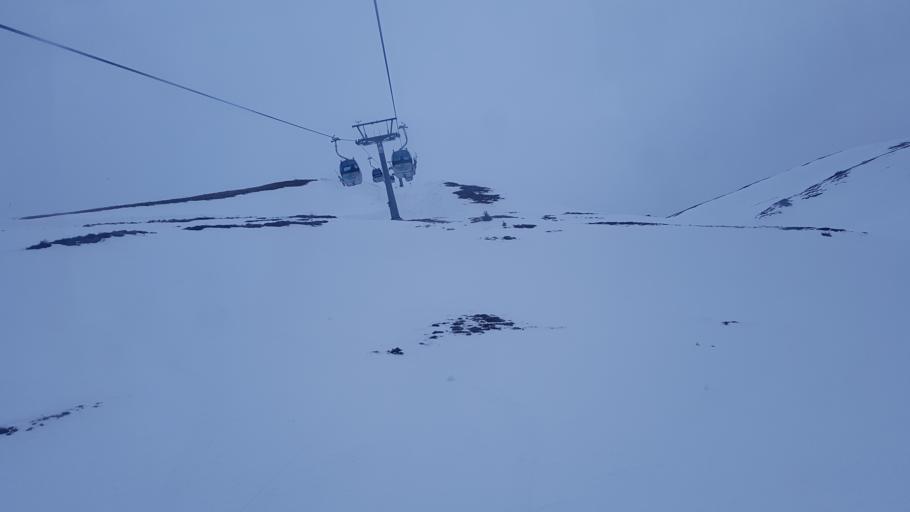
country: AT
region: Salzburg
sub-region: Politischer Bezirk Zell am See
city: Neukirchen am Grossvenediger
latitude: 47.2765
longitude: 12.2813
